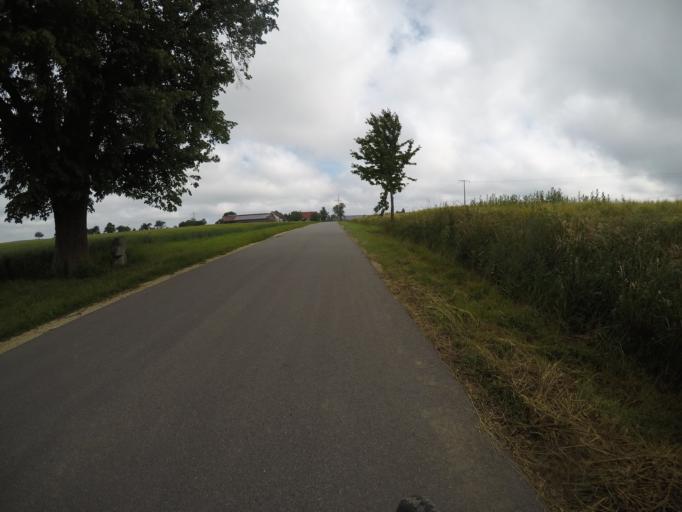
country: DE
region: Baden-Wuerttemberg
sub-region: Tuebingen Region
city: Dornstadt
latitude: 48.4888
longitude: 9.9523
